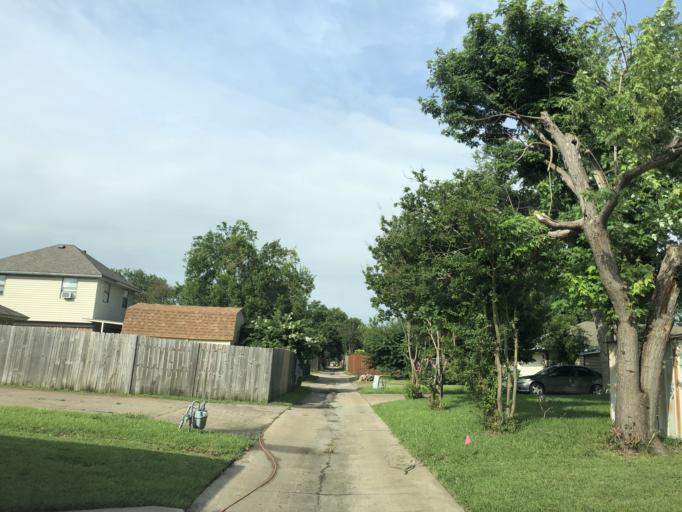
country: US
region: Texas
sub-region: Dallas County
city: Sunnyvale
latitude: 32.8446
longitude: -96.6127
